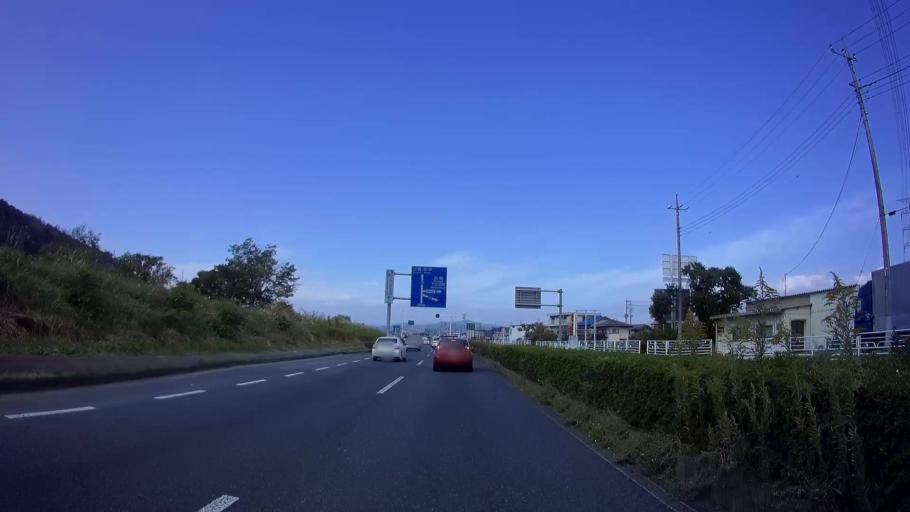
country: JP
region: Gunma
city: Takasaki
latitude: 36.3315
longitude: 138.9694
